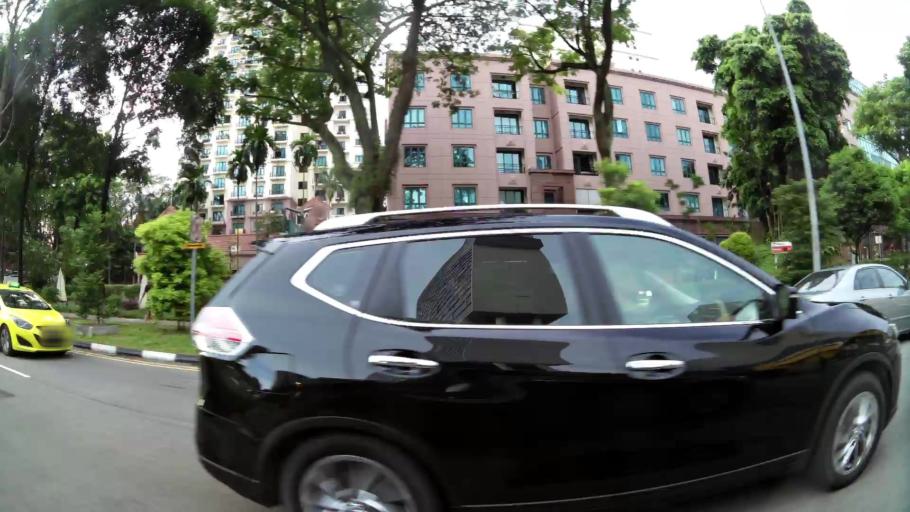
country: SG
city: Singapore
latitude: 1.2881
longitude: 103.8051
